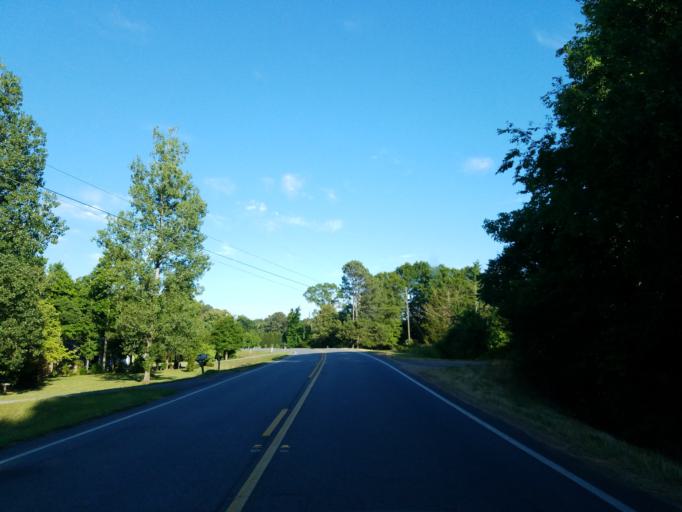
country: US
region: Georgia
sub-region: Gordon County
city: Calhoun
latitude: 34.5414
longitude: -84.9979
